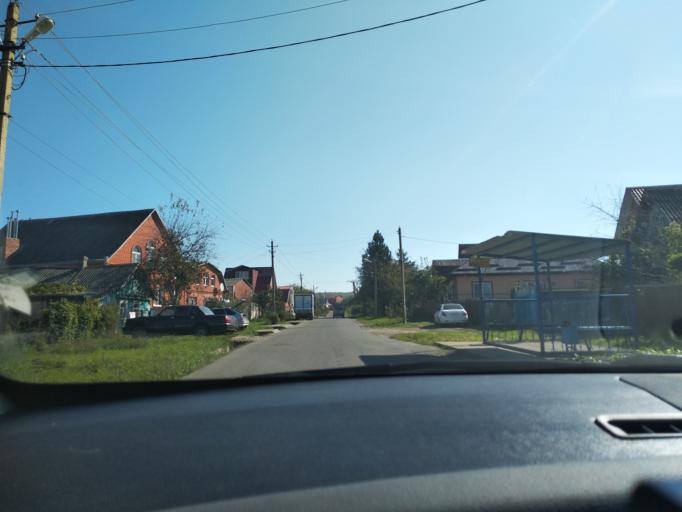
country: RU
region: Krasnodarskiy
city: Goryachiy Klyuch
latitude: 44.6323
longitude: 39.1498
